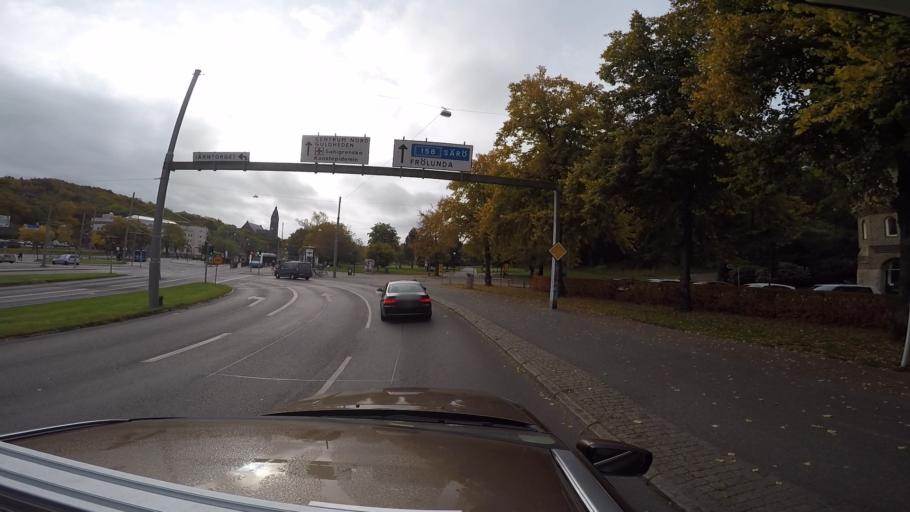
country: SE
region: Vaestra Goetaland
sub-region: Goteborg
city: Goeteborg
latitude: 57.6909
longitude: 11.9517
